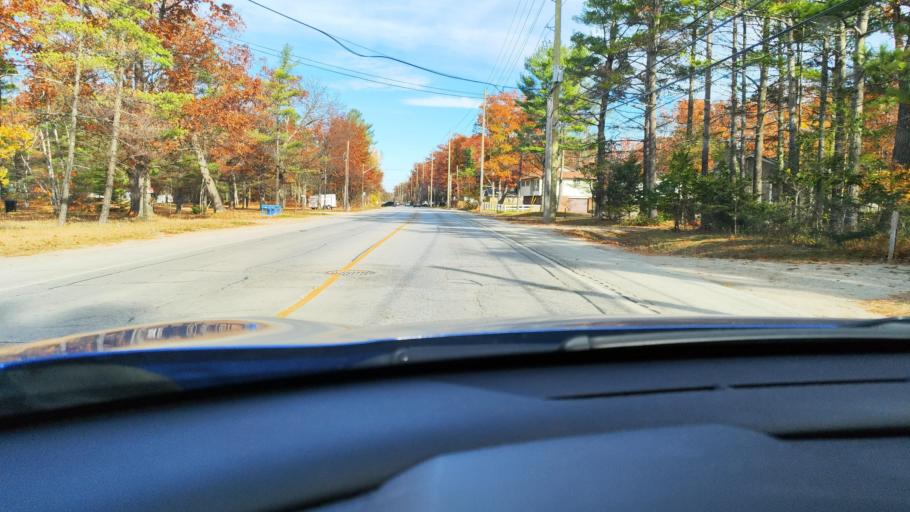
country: CA
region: Ontario
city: Wasaga Beach
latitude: 44.5028
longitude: -80.0346
